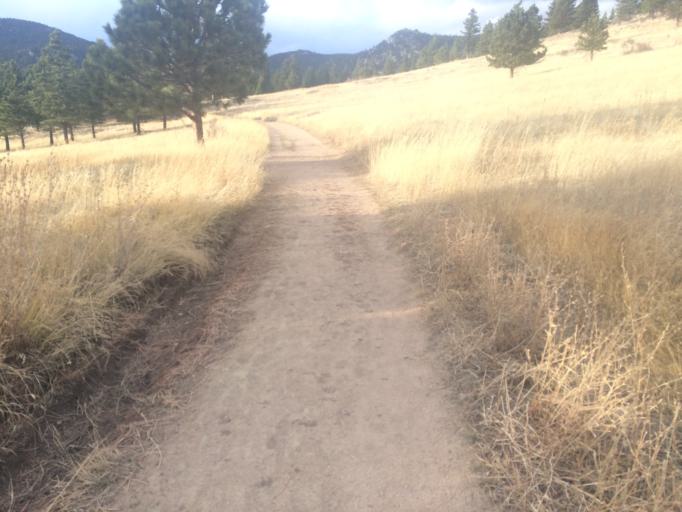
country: US
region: Colorado
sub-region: Boulder County
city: Coal Creek
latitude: 39.9594
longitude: -105.3420
